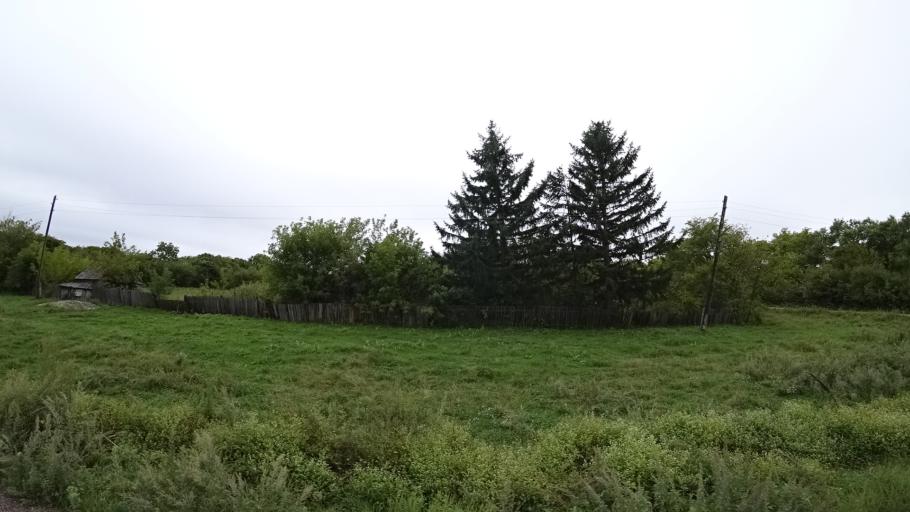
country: RU
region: Primorskiy
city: Monastyrishche
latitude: 44.0825
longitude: 132.5896
